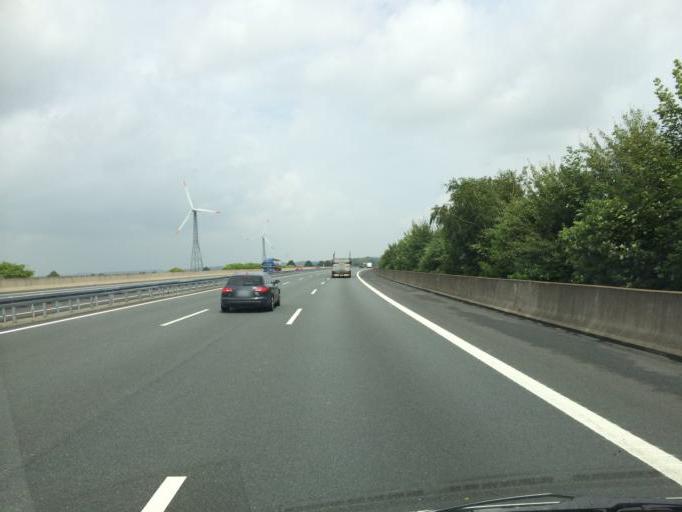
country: DE
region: Lower Saxony
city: Pohle
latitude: 52.2487
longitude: 9.2913
